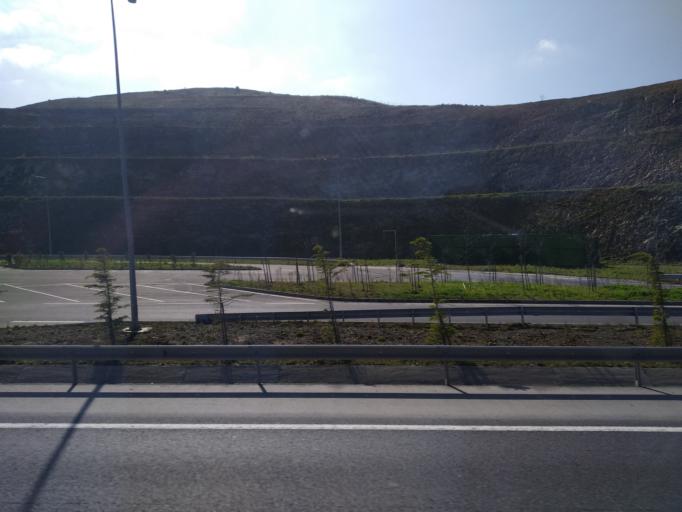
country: TR
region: Istanbul
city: Arikoey
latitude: 41.2255
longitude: 28.9839
